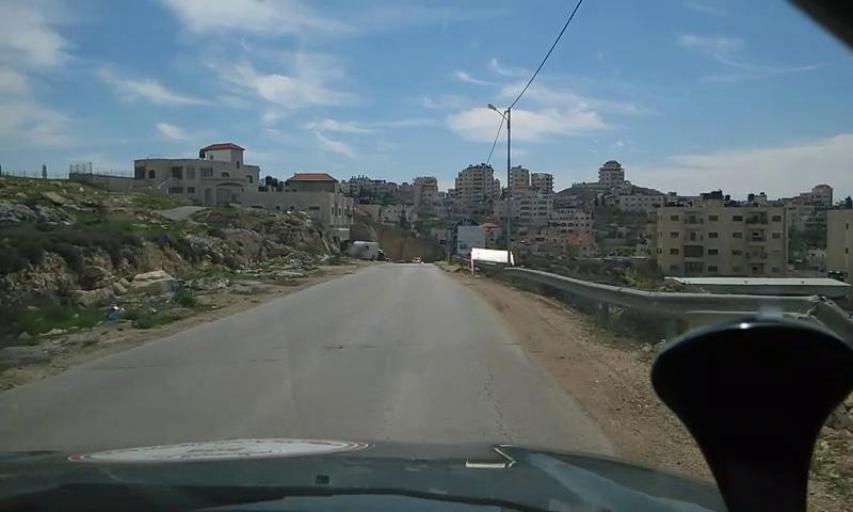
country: PS
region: West Bank
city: Bir Nabala
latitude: 31.8542
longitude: 35.2016
